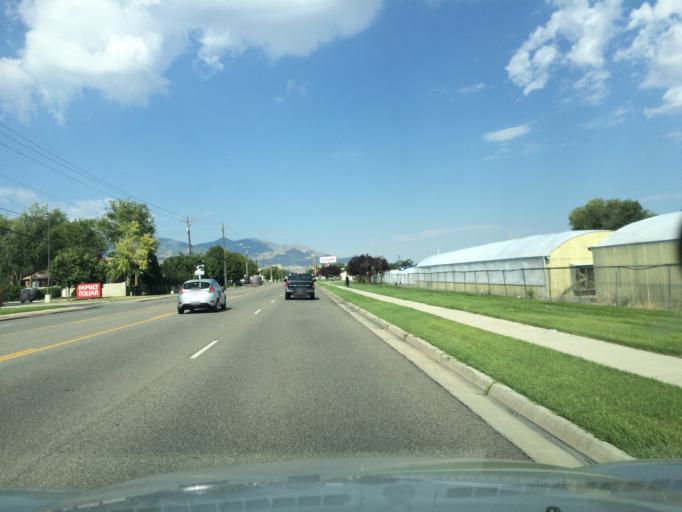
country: US
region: Utah
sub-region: Salt Lake County
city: West Valley City
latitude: 40.6966
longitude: -112.0025
